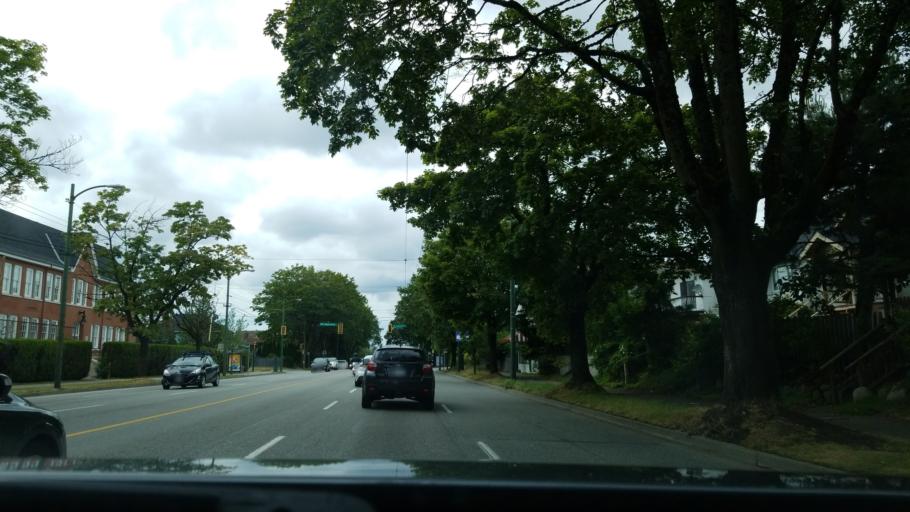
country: CA
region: British Columbia
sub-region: Fraser Valley Regional District
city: North Vancouver
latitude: 49.2623
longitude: -123.0606
